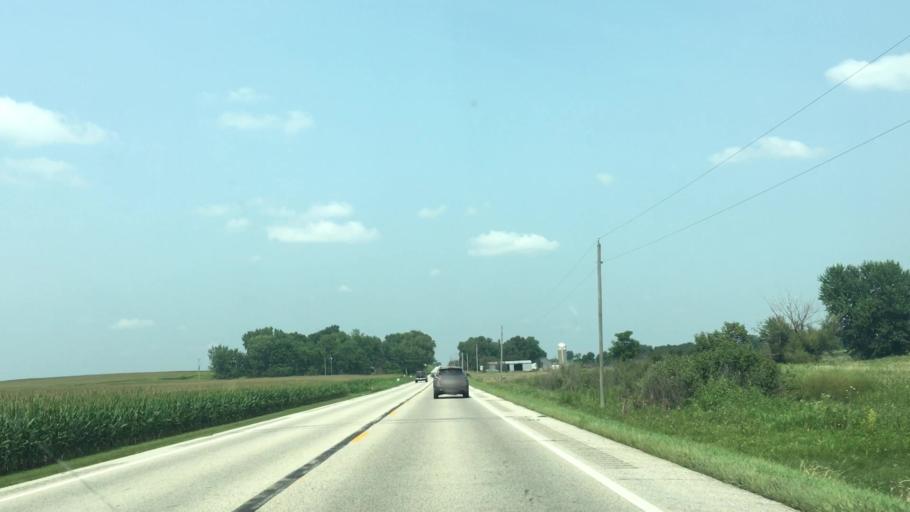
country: US
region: Iowa
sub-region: Buchanan County
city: Independence
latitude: 42.5256
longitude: -91.8899
